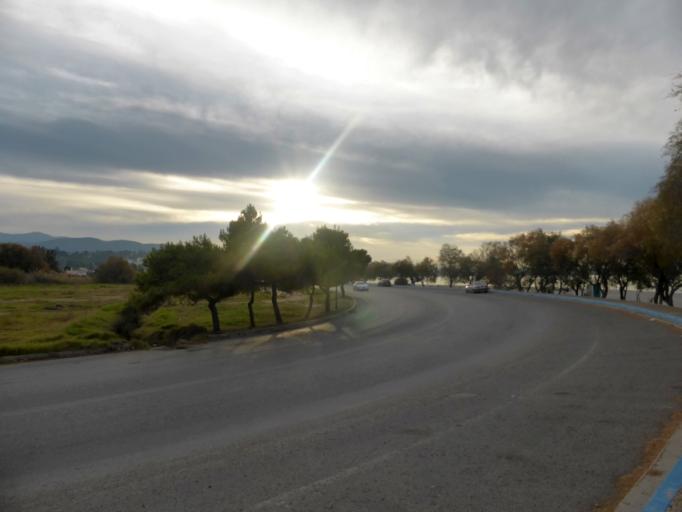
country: GR
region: Attica
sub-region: Nomarchia Anatolikis Attikis
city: Nea Palatia
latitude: 38.3281
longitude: 23.8080
